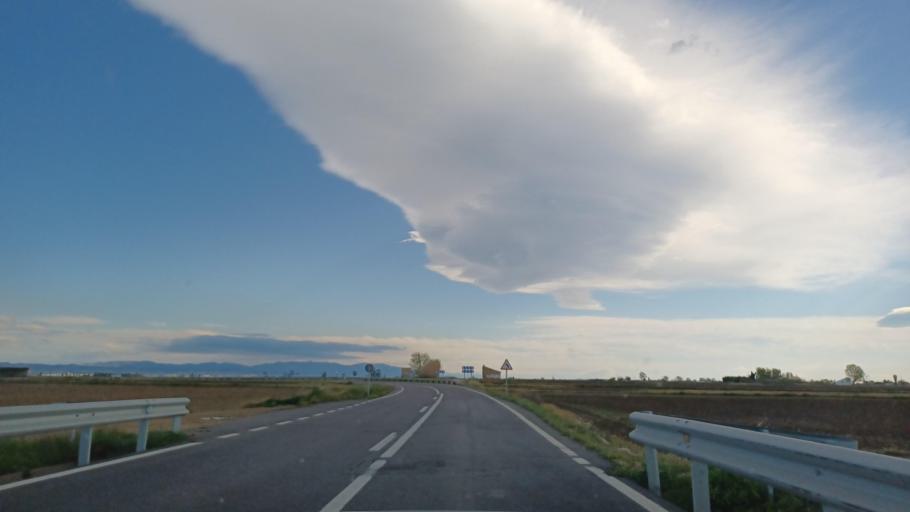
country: ES
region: Catalonia
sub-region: Provincia de Tarragona
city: Deltebre
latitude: 40.7363
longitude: 0.7135
